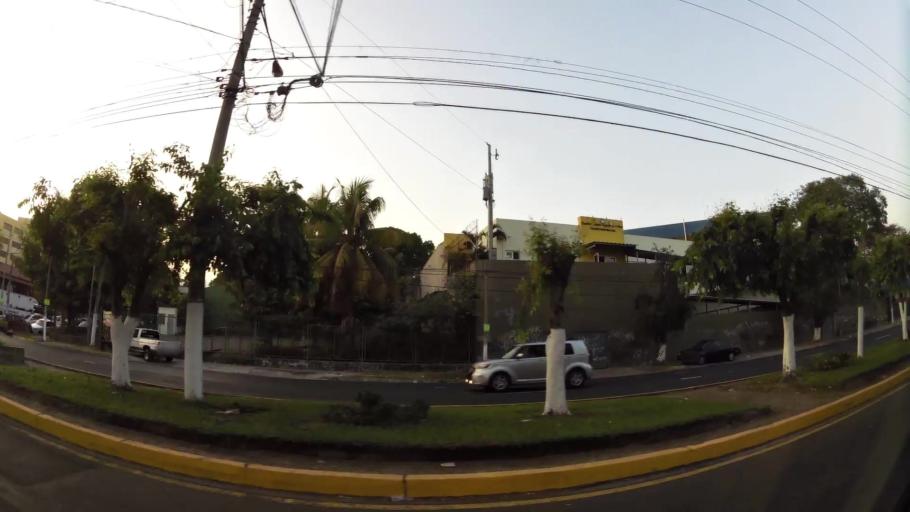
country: SV
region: San Salvador
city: Mejicanos
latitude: 13.7130
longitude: -89.2056
